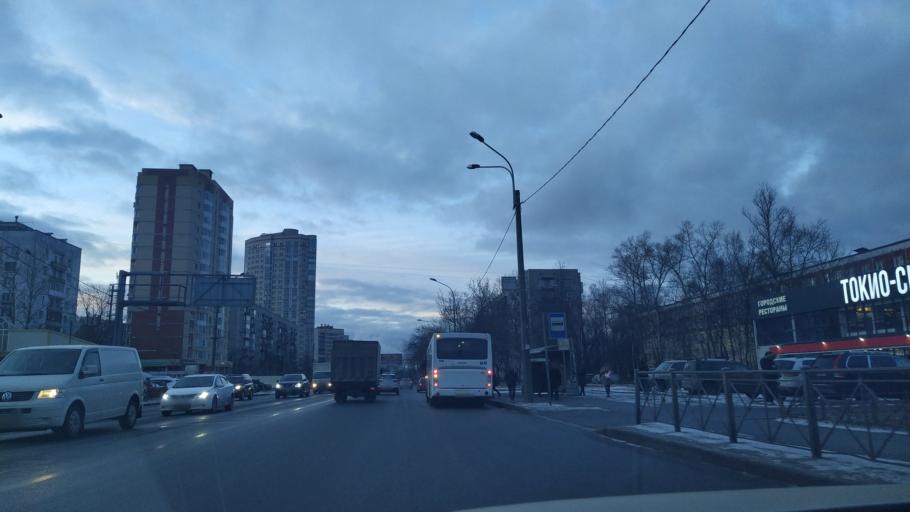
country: RU
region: St.-Petersburg
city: Dachnoye
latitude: 59.8419
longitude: 30.2550
